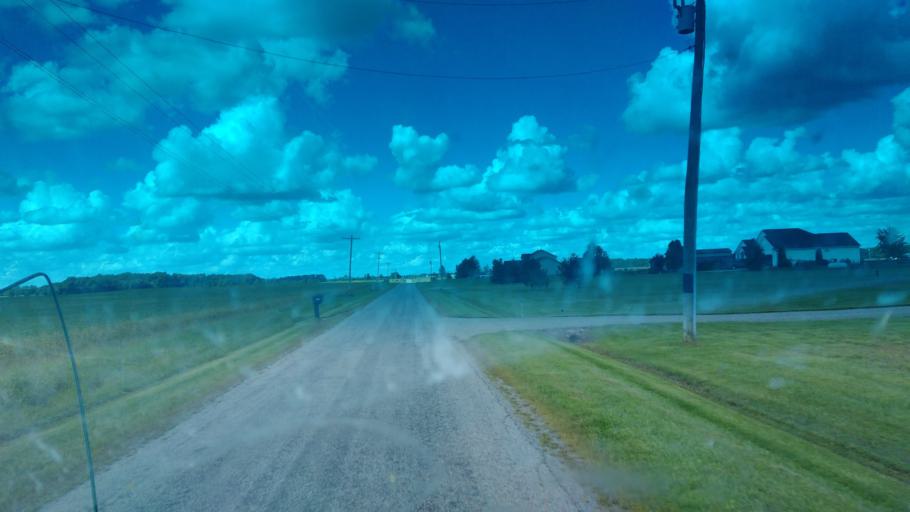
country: US
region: Ohio
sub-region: Union County
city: Richwood
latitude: 40.4557
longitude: -83.4948
